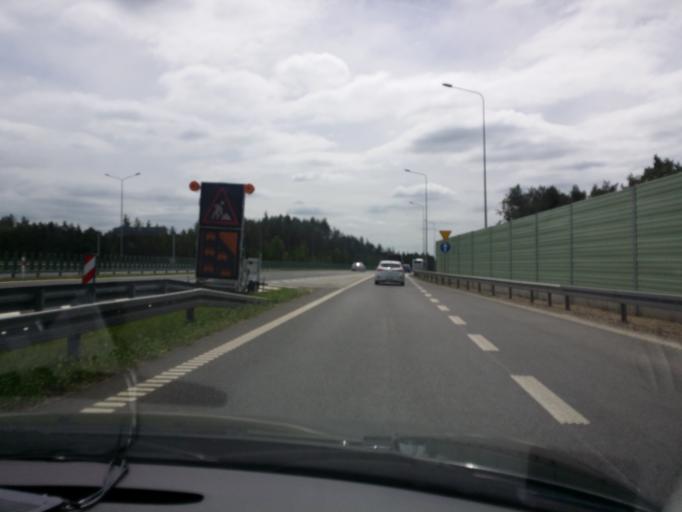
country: PL
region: Masovian Voivodeship
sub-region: Powiat szydlowiecki
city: Oronsko
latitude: 51.3287
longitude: 21.0164
